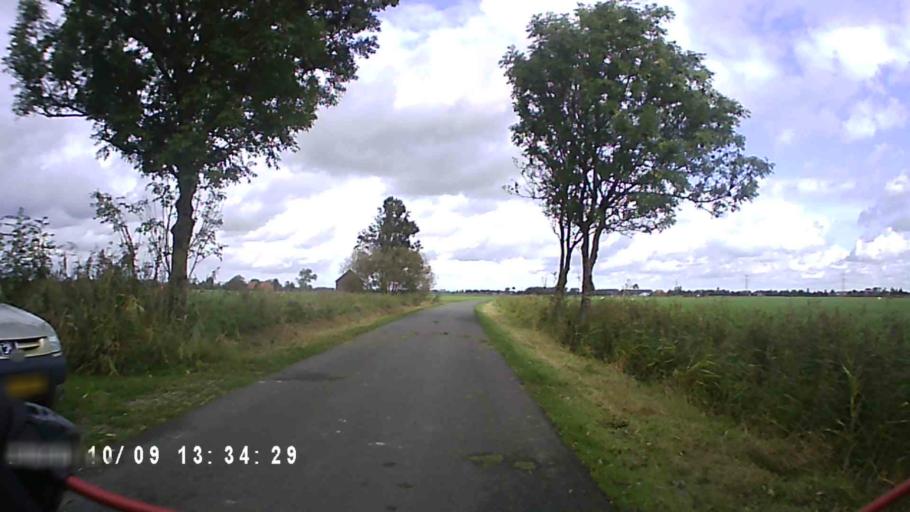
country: NL
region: Groningen
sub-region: Gemeente Zuidhorn
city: Aduard
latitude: 53.2924
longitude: 6.4694
